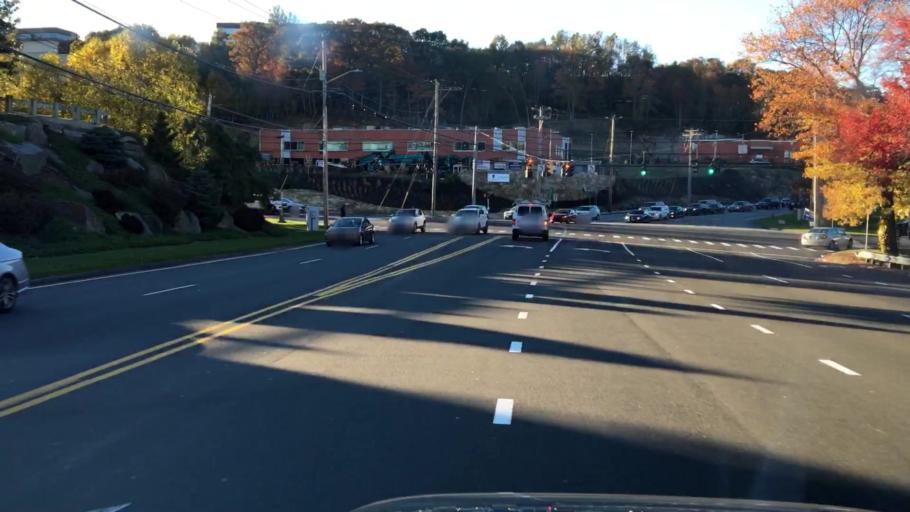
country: US
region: Connecticut
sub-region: Fairfield County
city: Shelton
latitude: 41.2767
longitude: -73.1213
